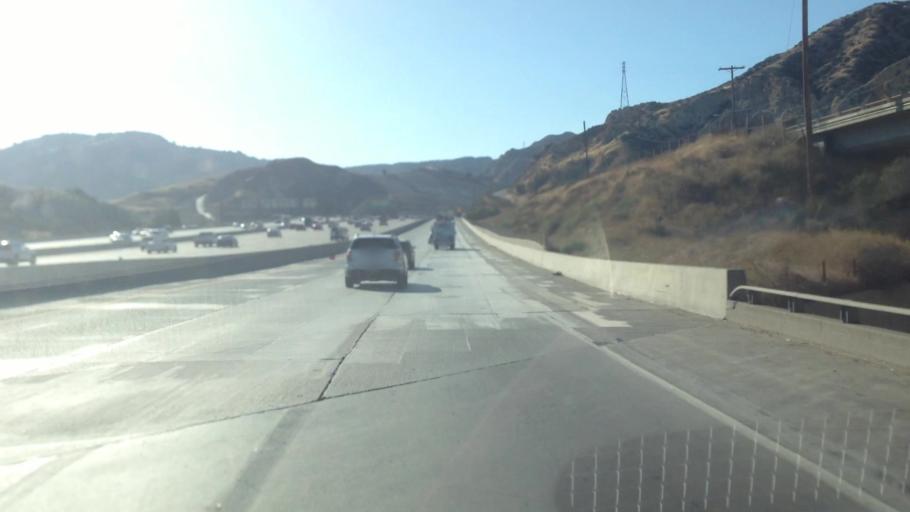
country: US
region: California
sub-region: Los Angeles County
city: San Fernando
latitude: 34.3215
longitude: -118.4963
